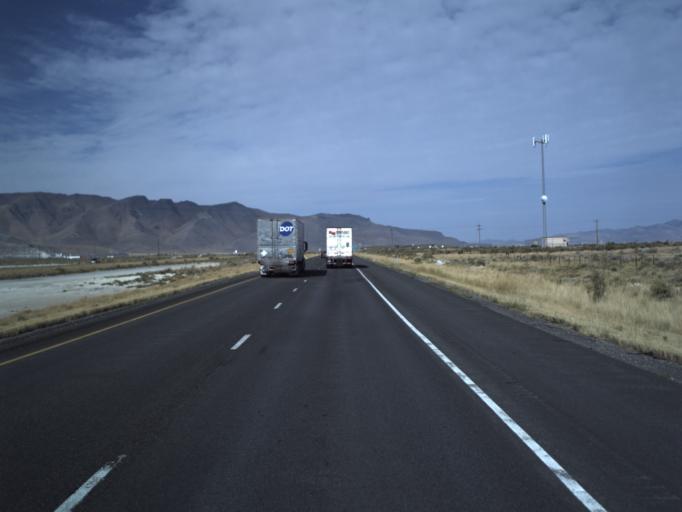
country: US
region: Utah
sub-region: Tooele County
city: Grantsville
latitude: 40.7049
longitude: -112.5100
